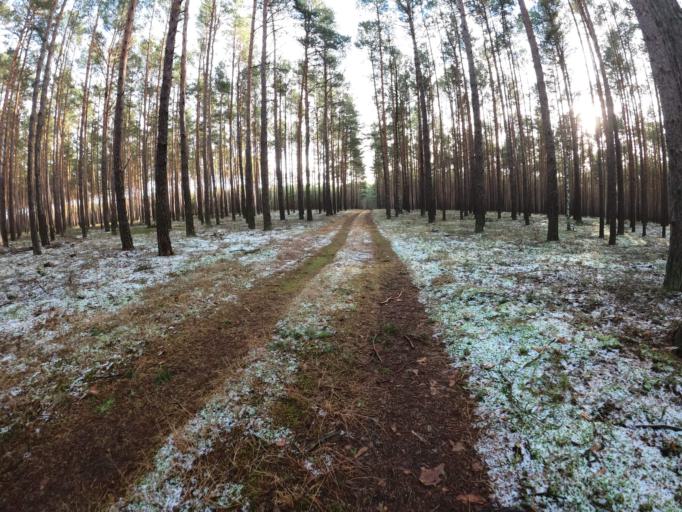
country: PL
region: Lubusz
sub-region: Powiat slubicki
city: Cybinka
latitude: 52.2394
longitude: 14.8231
